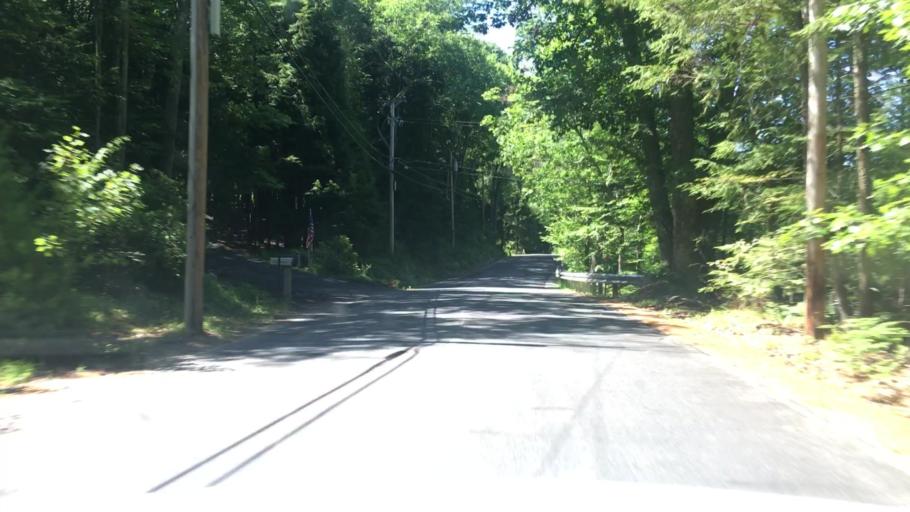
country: US
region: New Hampshire
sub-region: Merrimack County
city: Hopkinton
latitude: 43.2409
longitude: -71.6241
